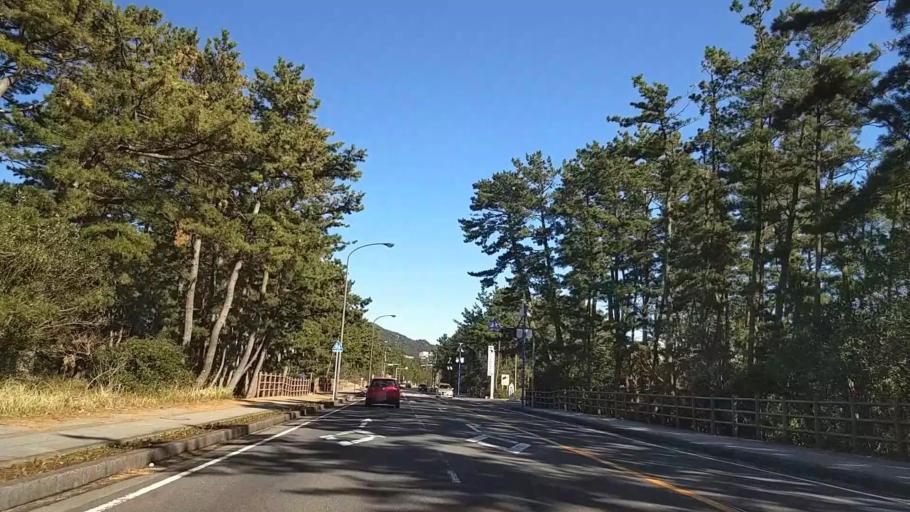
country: JP
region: Chiba
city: Kawaguchi
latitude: 35.1141
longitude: 140.1164
